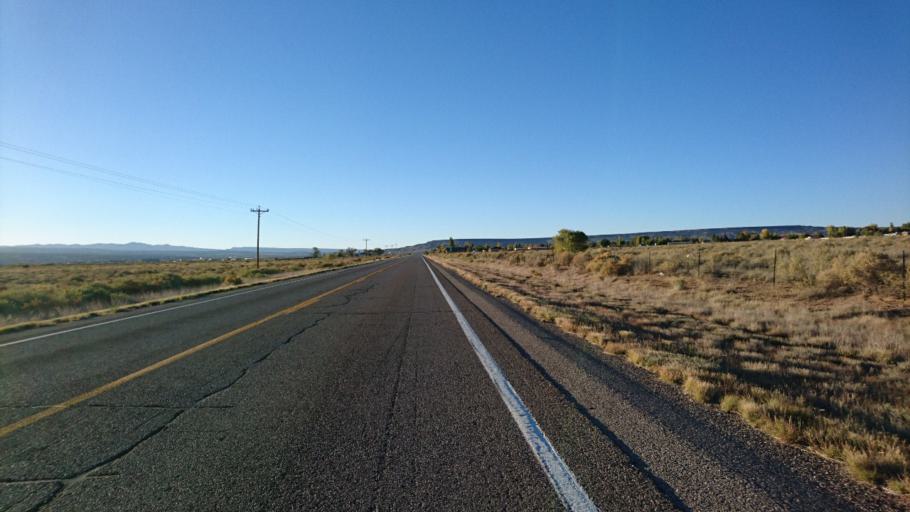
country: US
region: New Mexico
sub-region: Cibola County
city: Grants
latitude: 35.1238
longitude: -107.7998
